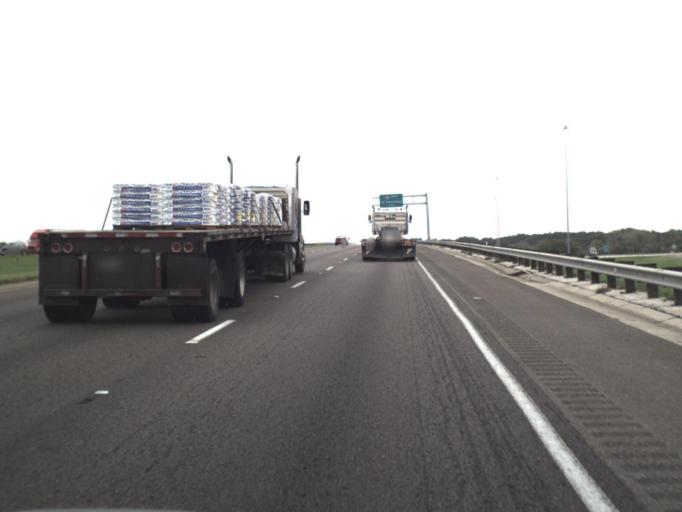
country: US
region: Florida
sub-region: Manatee County
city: Ellenton
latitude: 27.6036
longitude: -82.5011
